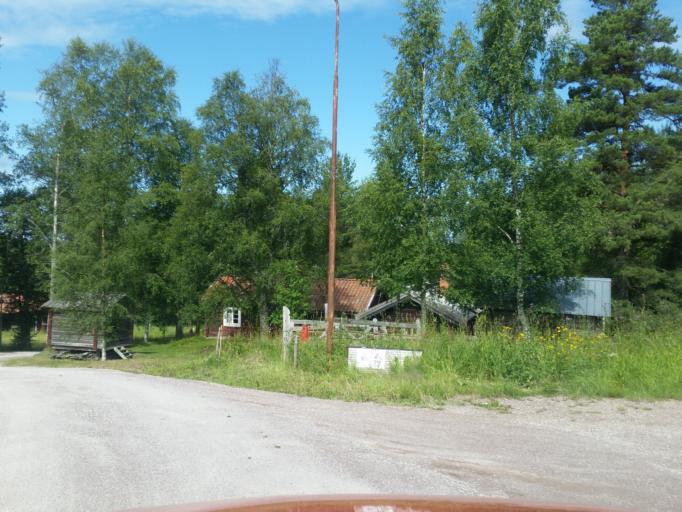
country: SE
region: Dalarna
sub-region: Gagnefs Kommun
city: Gagnef
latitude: 60.6594
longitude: 15.1224
